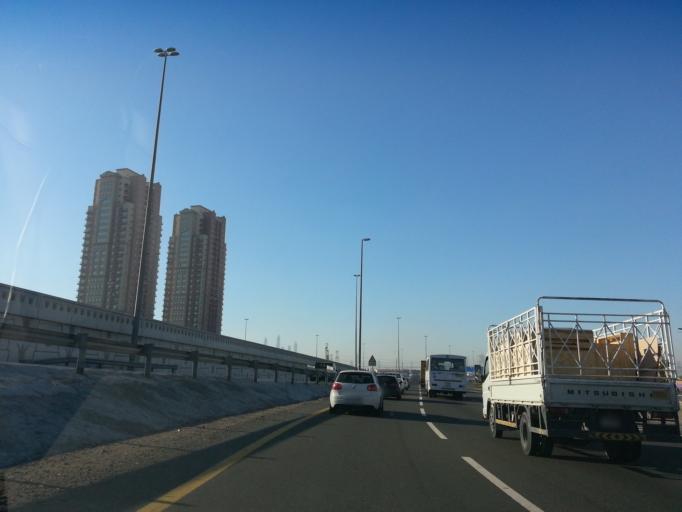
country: AE
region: Dubai
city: Dubai
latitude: 25.0462
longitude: 55.1986
